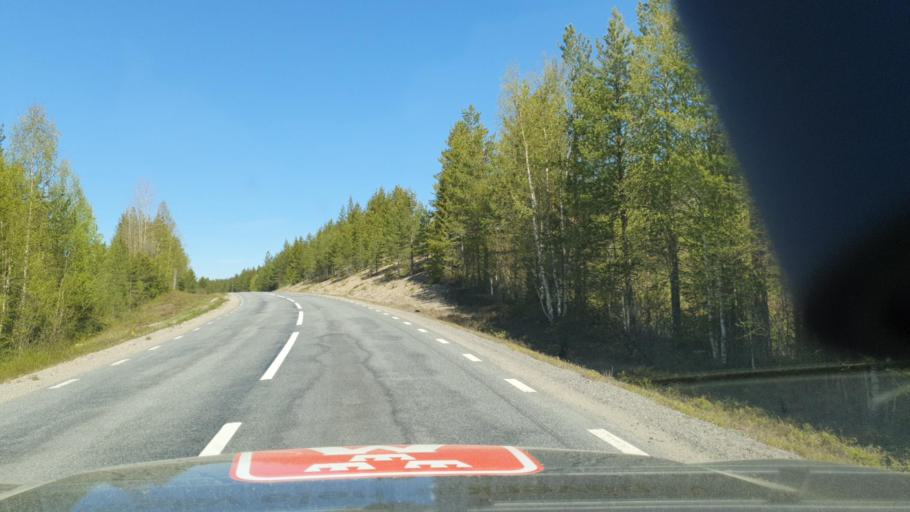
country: SE
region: Vaesternorrland
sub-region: OErnskoeldsviks Kommun
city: Bredbyn
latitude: 63.7377
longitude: 18.5009
